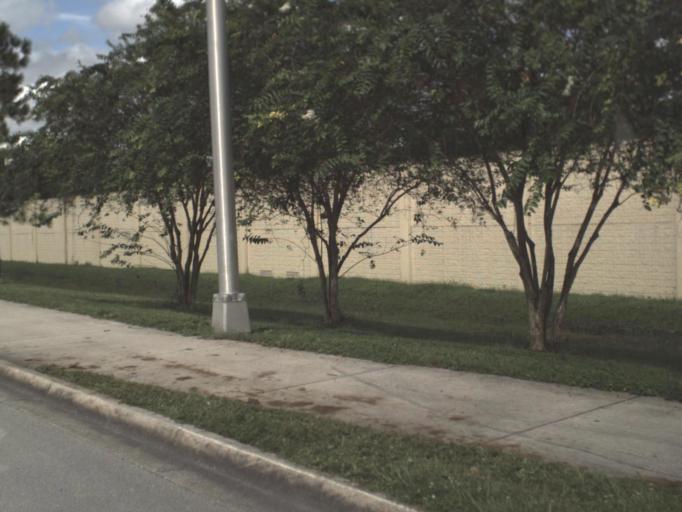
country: US
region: Florida
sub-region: Lee County
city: Palmona Park
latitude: 26.6934
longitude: -81.8883
